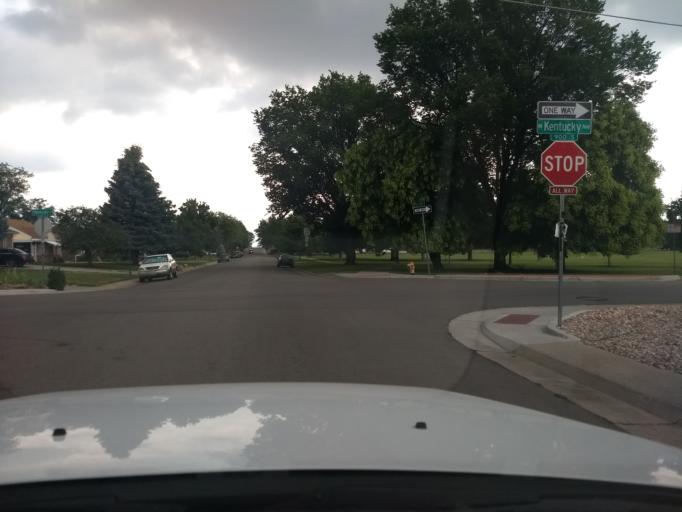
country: US
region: Colorado
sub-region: Denver County
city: Denver
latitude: 39.7004
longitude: -105.0203
